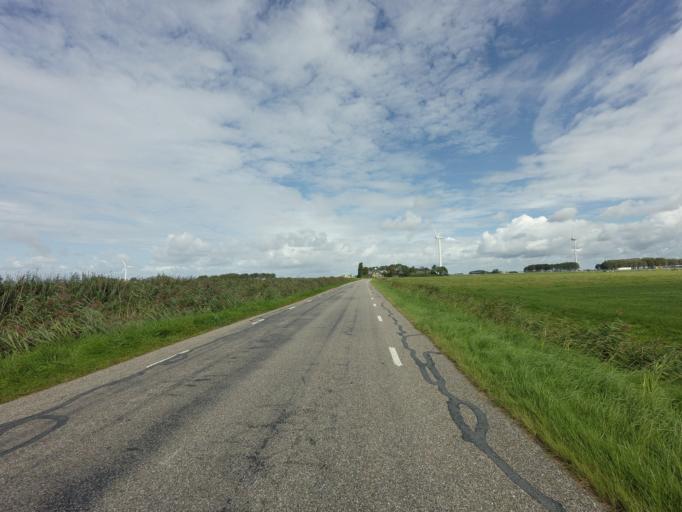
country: NL
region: Friesland
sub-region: Sudwest Fryslan
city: Makkum
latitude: 53.0879
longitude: 5.4211
